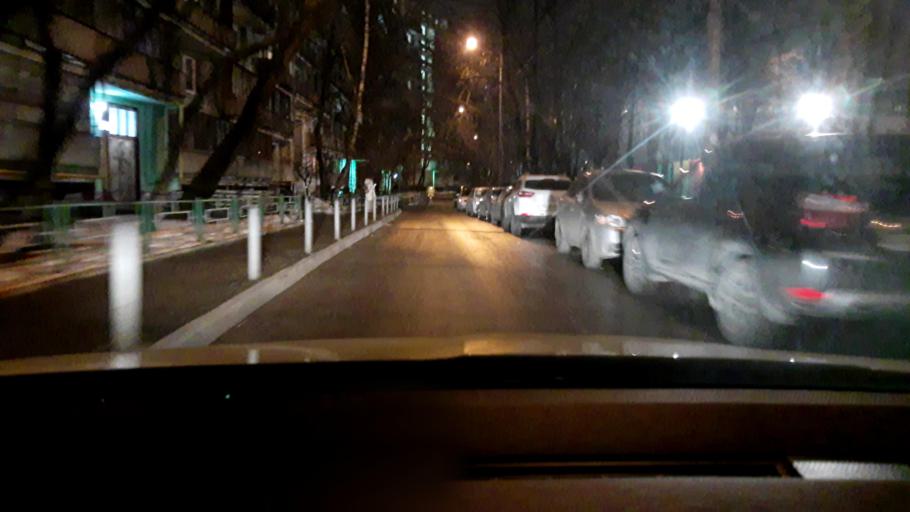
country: RU
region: Moscow
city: Orekhovo-Borisovo
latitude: 55.6119
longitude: 37.7062
